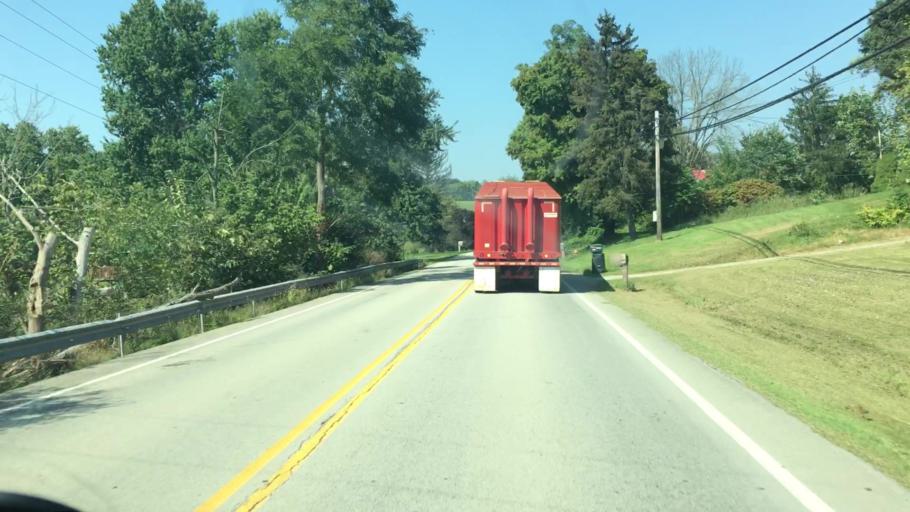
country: US
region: Pennsylvania
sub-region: Washington County
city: Washington
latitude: 40.1035
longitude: -80.2916
